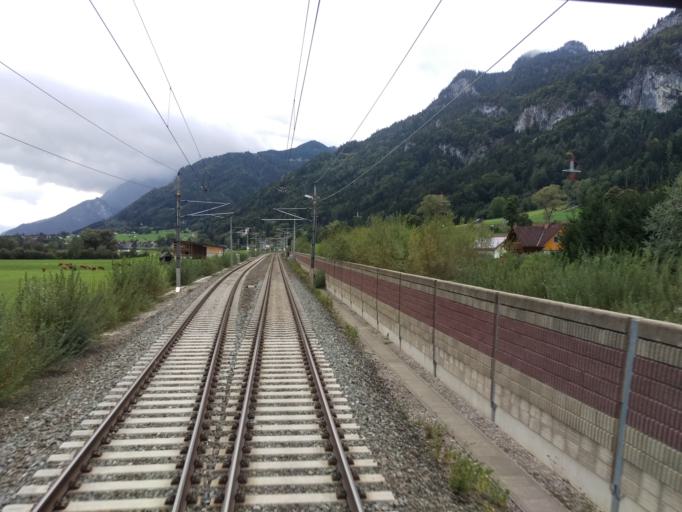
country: AT
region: Styria
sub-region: Politischer Bezirk Liezen
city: Worschach
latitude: 47.5454
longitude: 14.1375
